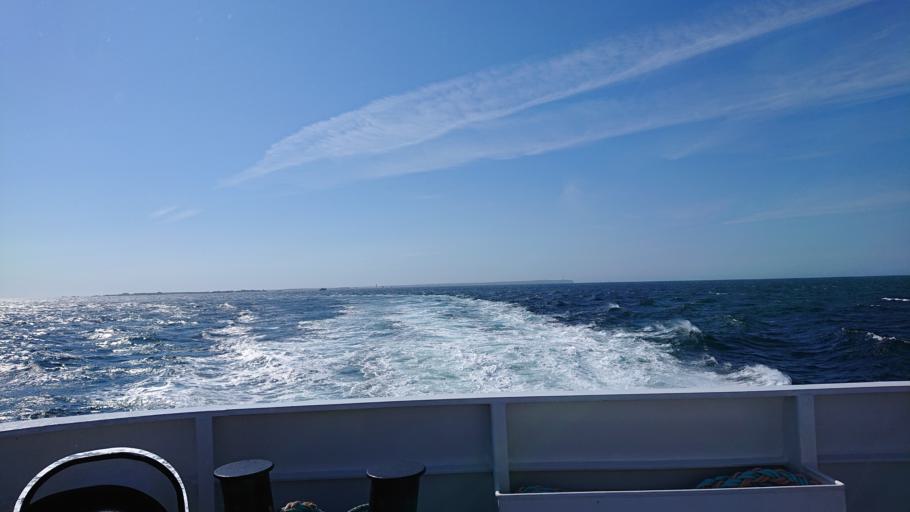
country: FR
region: Brittany
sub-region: Departement du Finistere
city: Le Conquet
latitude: 48.4145
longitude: -4.9397
